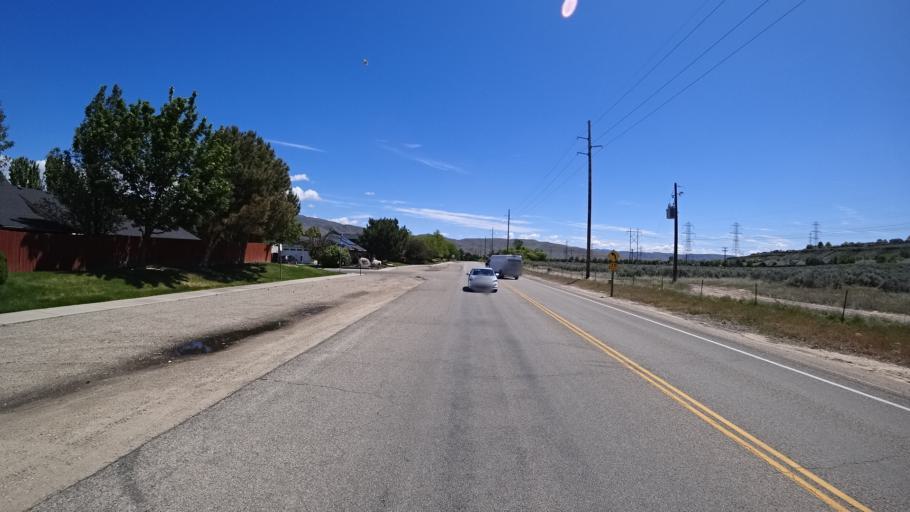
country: US
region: Idaho
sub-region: Ada County
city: Boise
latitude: 43.5605
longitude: -116.1366
